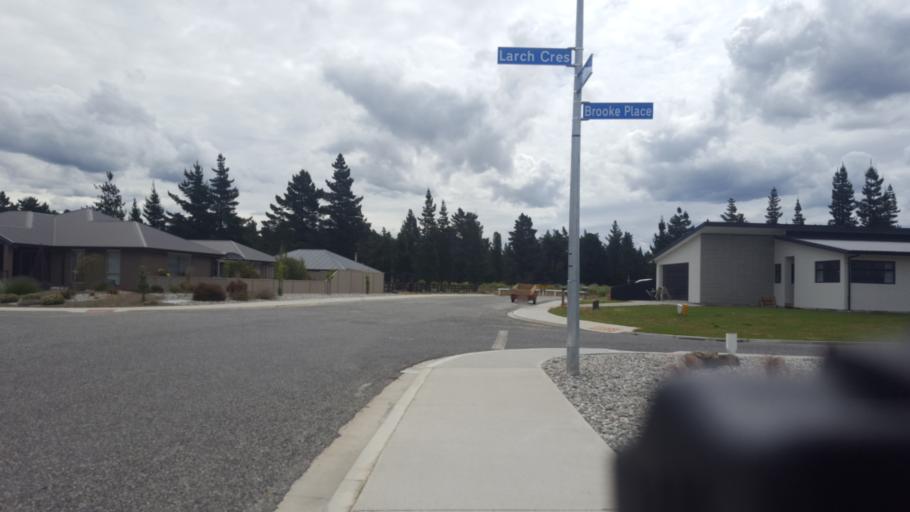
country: NZ
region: Otago
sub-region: Queenstown-Lakes District
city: Wanaka
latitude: -45.2432
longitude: 169.3751
